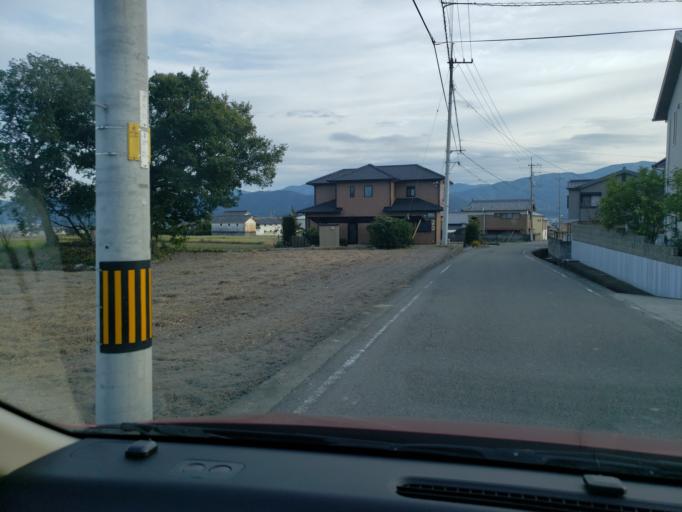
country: JP
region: Tokushima
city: Wakimachi
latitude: 34.0888
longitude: 134.2267
